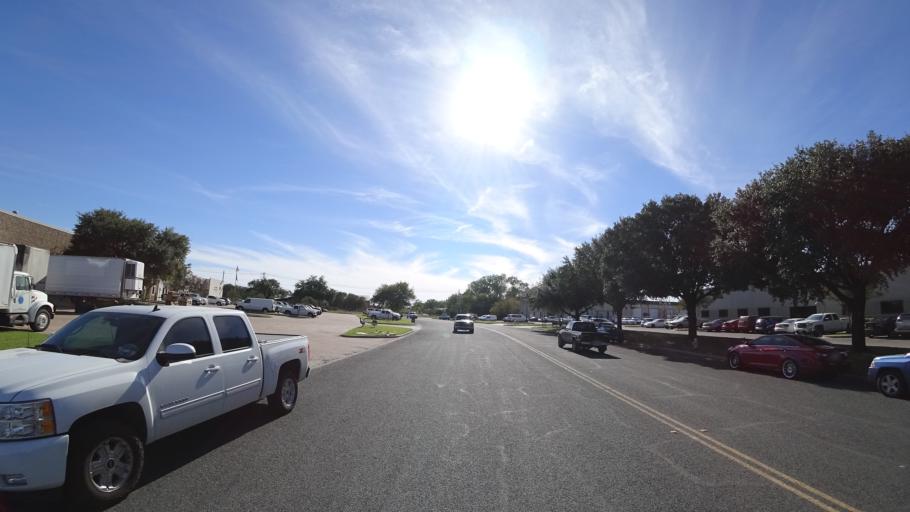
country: US
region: Texas
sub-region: Travis County
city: Austin
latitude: 30.2553
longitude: -97.6805
